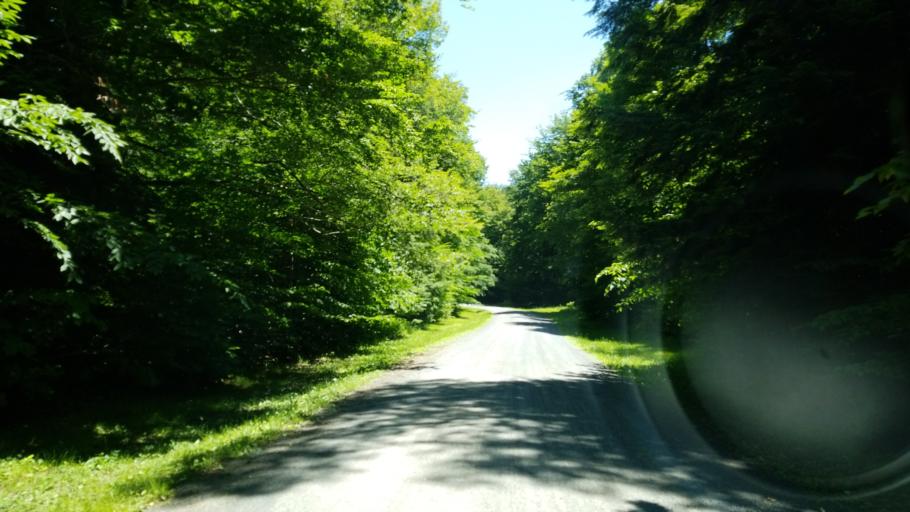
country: US
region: Pennsylvania
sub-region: Clearfield County
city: Shiloh
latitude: 41.2631
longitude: -78.2598
